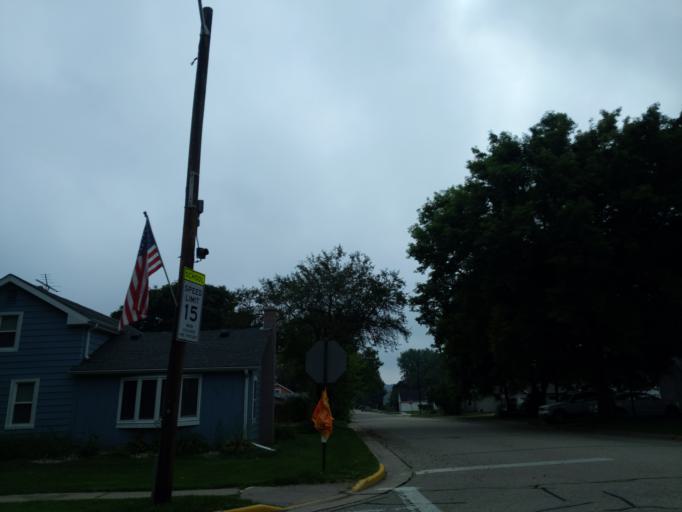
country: US
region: Wisconsin
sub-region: Dane County
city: Black Earth
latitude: 43.1354
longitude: -89.7480
